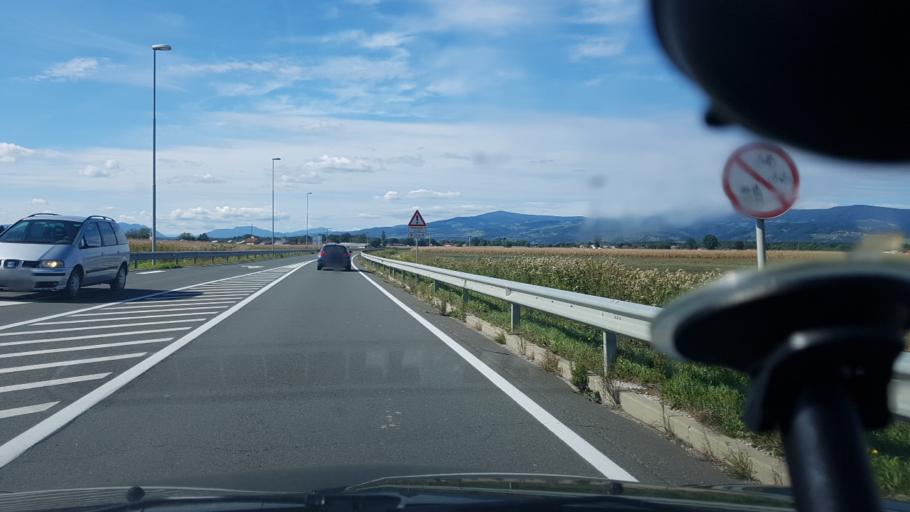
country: SI
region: Slovenska Bistrica
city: Pragersko
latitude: 46.4084
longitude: 15.7064
